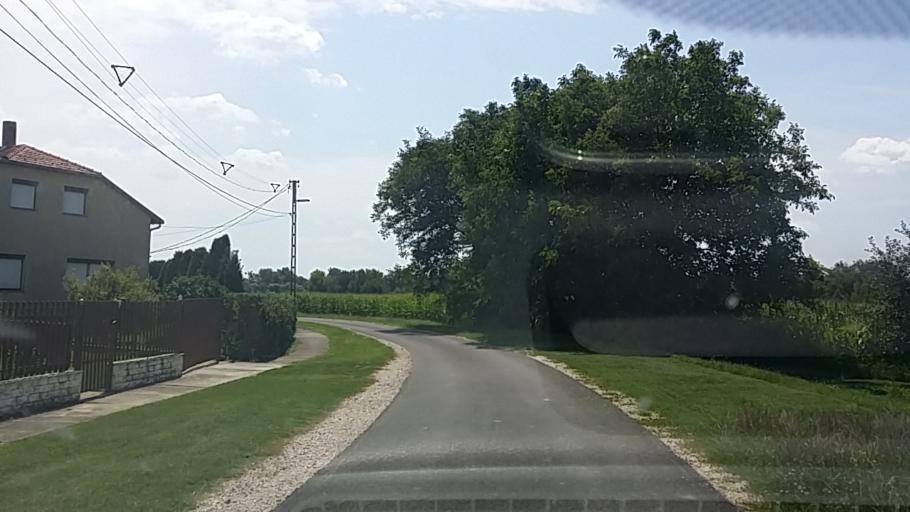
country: HR
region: Medimurska
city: Kotoriba
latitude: 46.3817
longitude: 16.8338
